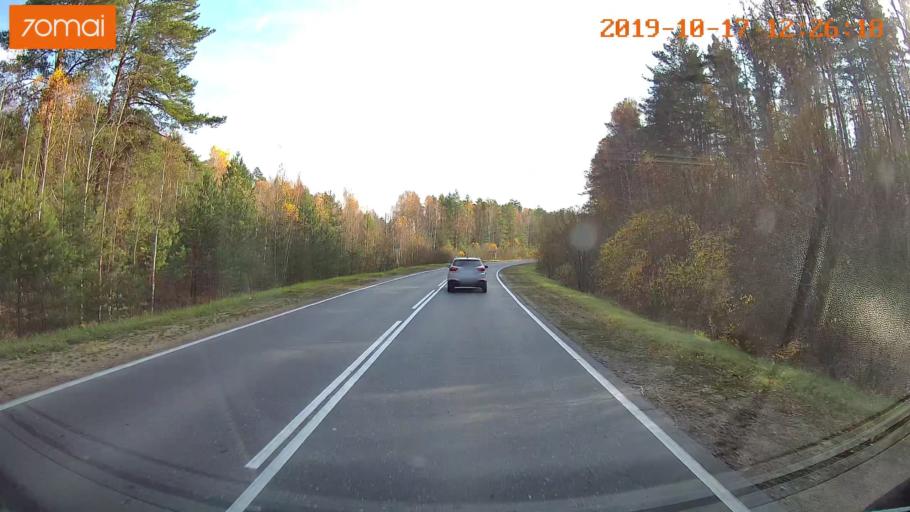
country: RU
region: Rjazan
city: Syntul
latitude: 55.0204
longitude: 41.2538
